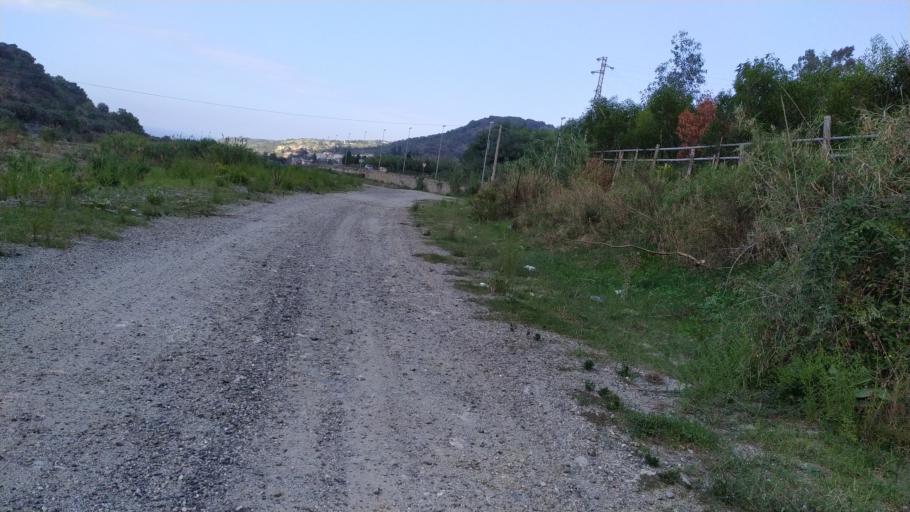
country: IT
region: Sicily
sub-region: Messina
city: Saponara
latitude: 38.1962
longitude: 15.4297
